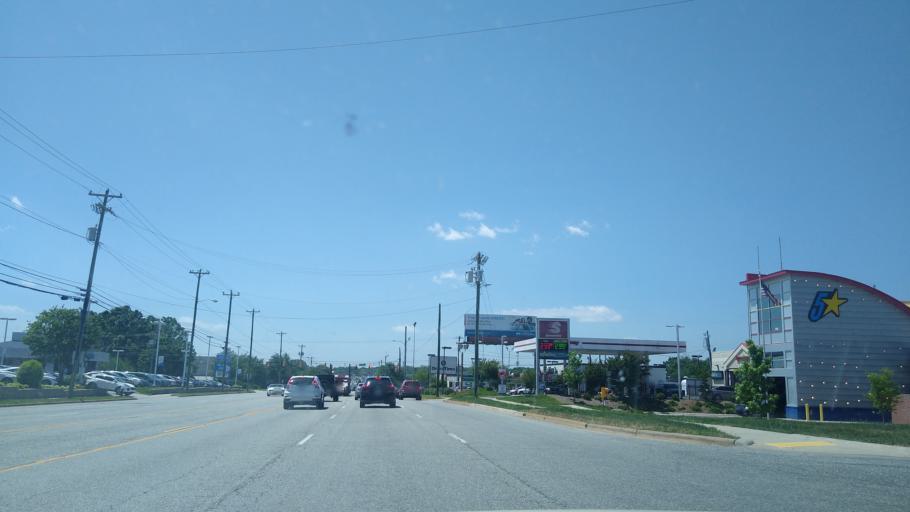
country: US
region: North Carolina
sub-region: Guilford County
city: Greensboro
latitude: 36.0604
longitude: -79.8693
